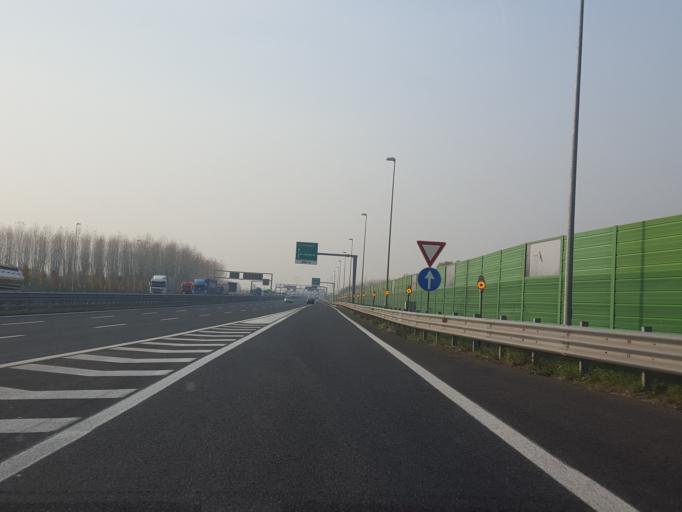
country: IT
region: Veneto
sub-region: Provincia di Venezia
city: Marcon-Gaggio-Colmello
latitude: 45.5890
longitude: 12.2875
